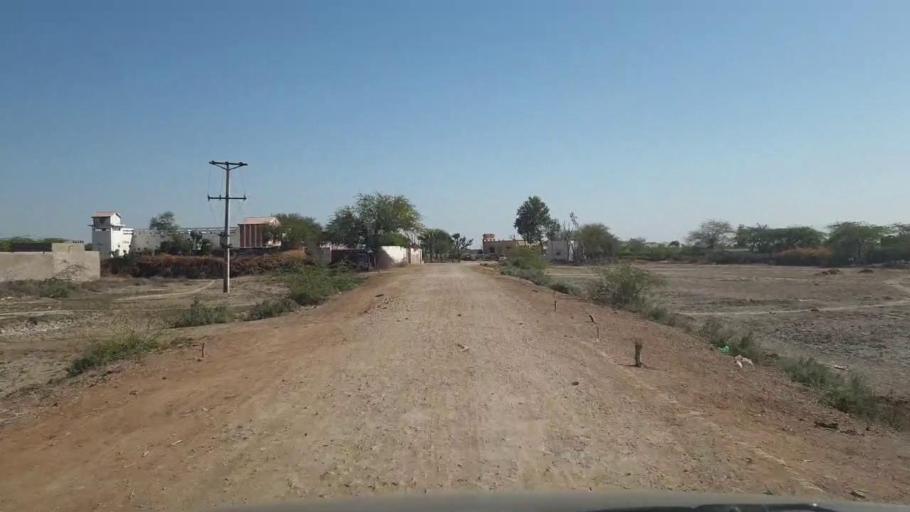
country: PK
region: Sindh
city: Dhoro Naro
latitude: 25.3846
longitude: 69.5984
